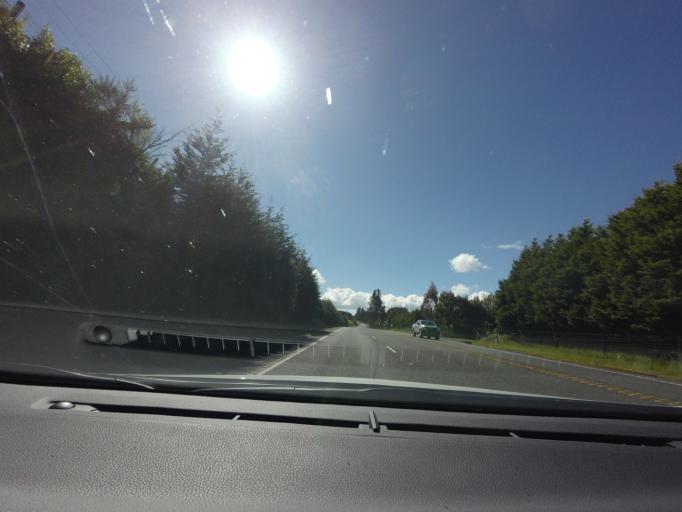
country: NZ
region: Bay of Plenty
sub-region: Rotorua District
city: Rotorua
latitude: -38.0636
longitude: 176.0986
